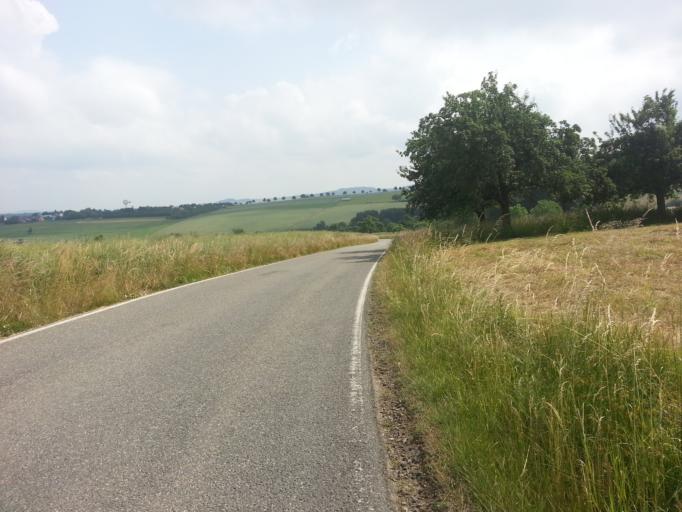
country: DE
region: Rheinland-Pfalz
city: Hunzel
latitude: 50.2604
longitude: 7.8299
